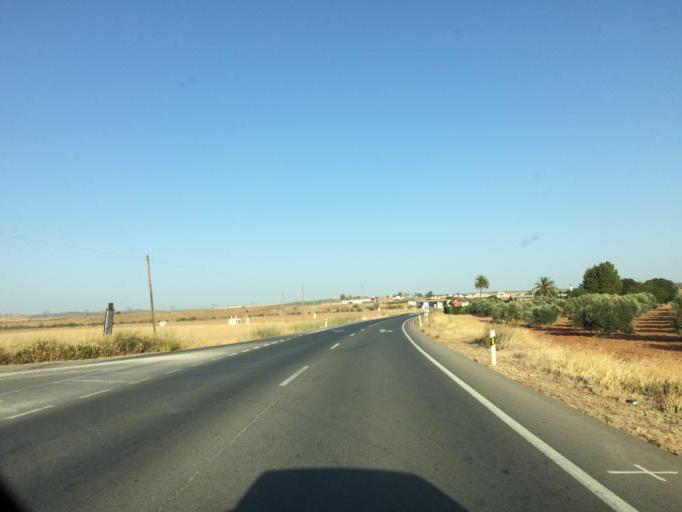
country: ES
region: Andalusia
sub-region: Provincia de Malaga
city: Humilladero
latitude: 37.0622
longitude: -4.7080
